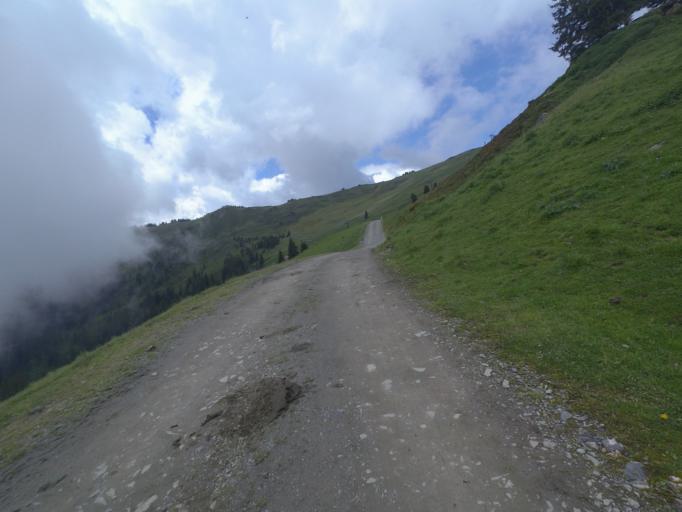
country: AT
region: Salzburg
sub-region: Politischer Bezirk Zell am See
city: Viehhofen
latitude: 47.4043
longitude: 12.7104
